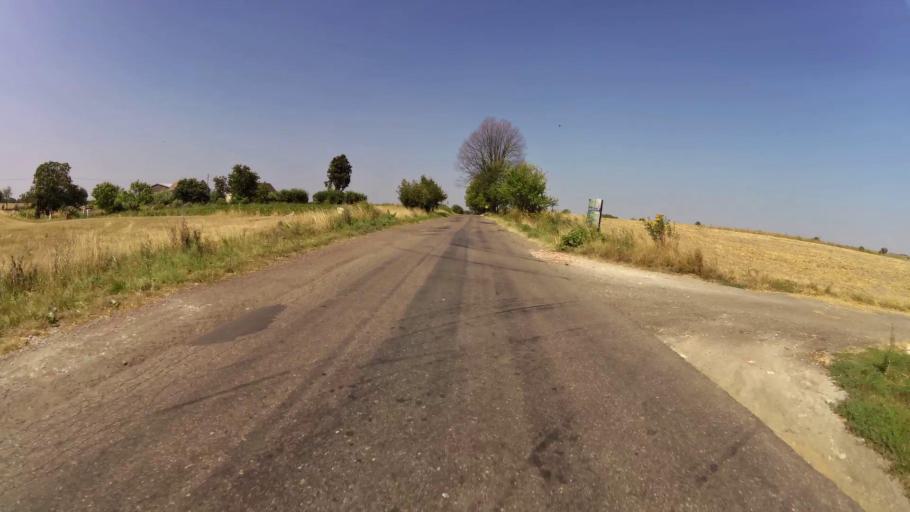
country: PL
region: West Pomeranian Voivodeship
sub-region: Powiat walecki
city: Walcz
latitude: 53.2231
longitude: 16.4676
